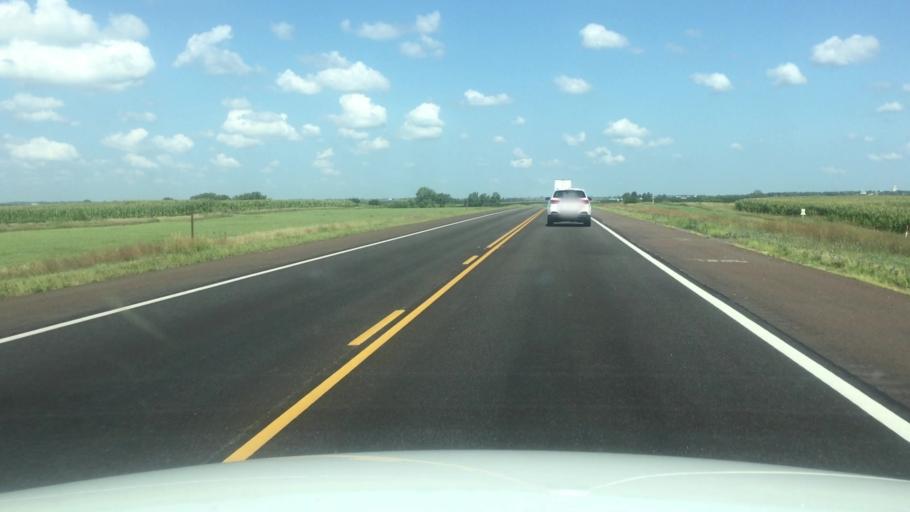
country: US
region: Kansas
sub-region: Nemaha County
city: Sabetha
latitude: 39.8645
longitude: -95.7692
